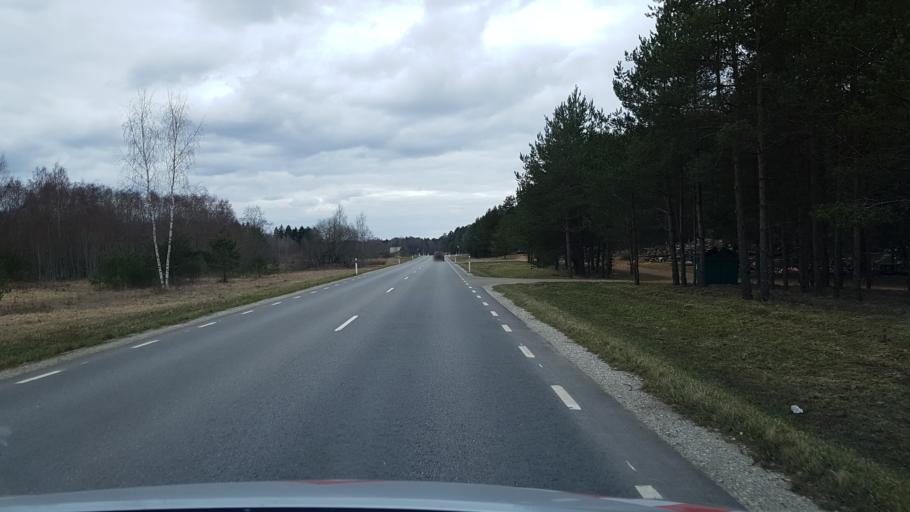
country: EE
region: Ida-Virumaa
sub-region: Narva-Joesuu linn
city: Narva-Joesuu
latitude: 59.4182
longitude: 28.1013
